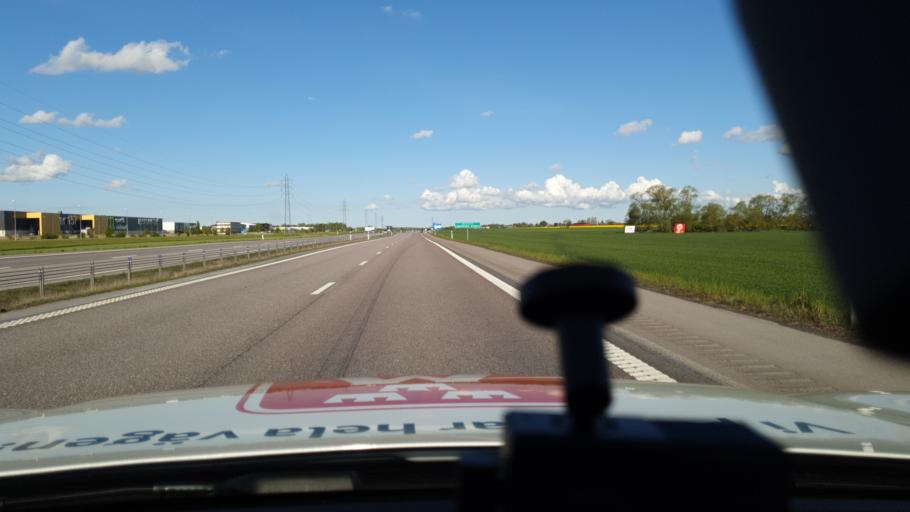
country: SE
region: OEstergoetland
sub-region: Linkopings Kommun
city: Linkoping
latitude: 58.4352
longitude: 15.6089
